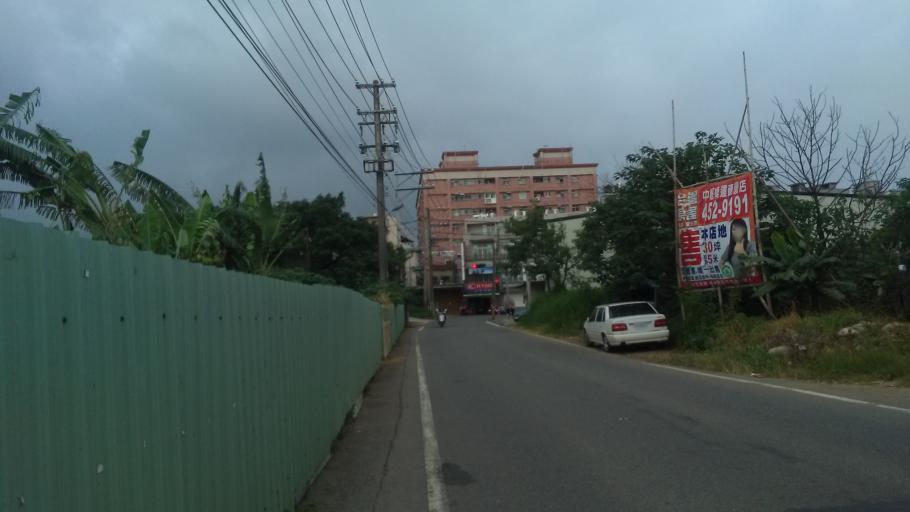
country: TW
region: Taiwan
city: Taoyuan City
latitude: 24.9554
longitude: 121.2615
